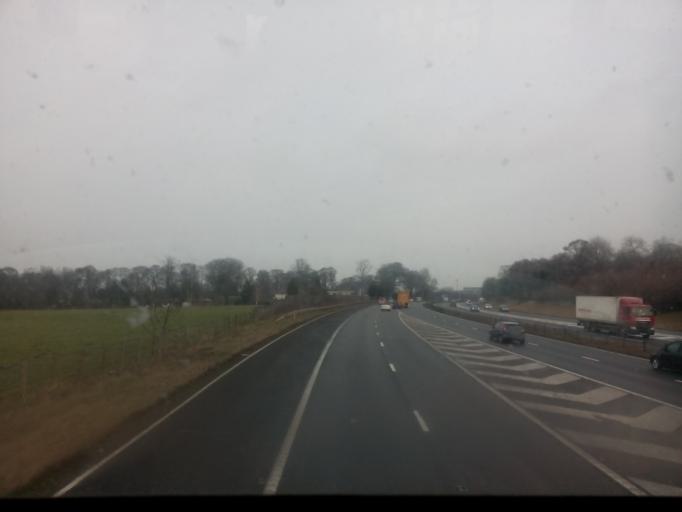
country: GB
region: England
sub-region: County Durham
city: Chester-le-Street
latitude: 54.8700
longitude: -1.5679
